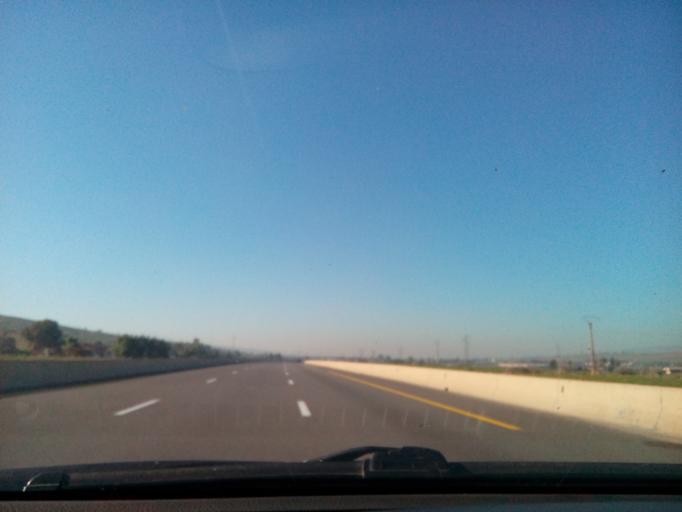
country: DZ
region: Chlef
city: Boukadir
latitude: 36.0372
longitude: 1.0852
